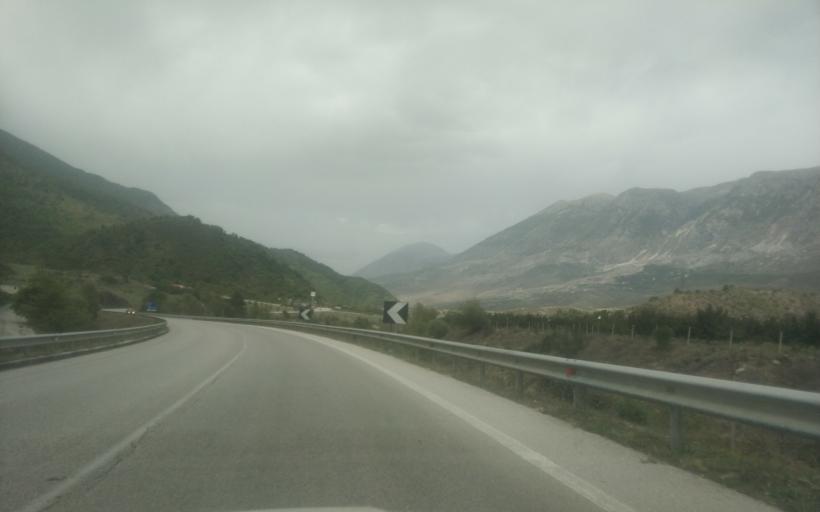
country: AL
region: Gjirokaster
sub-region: Rrethi i Gjirokastres
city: Picar
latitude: 40.2034
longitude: 20.0914
